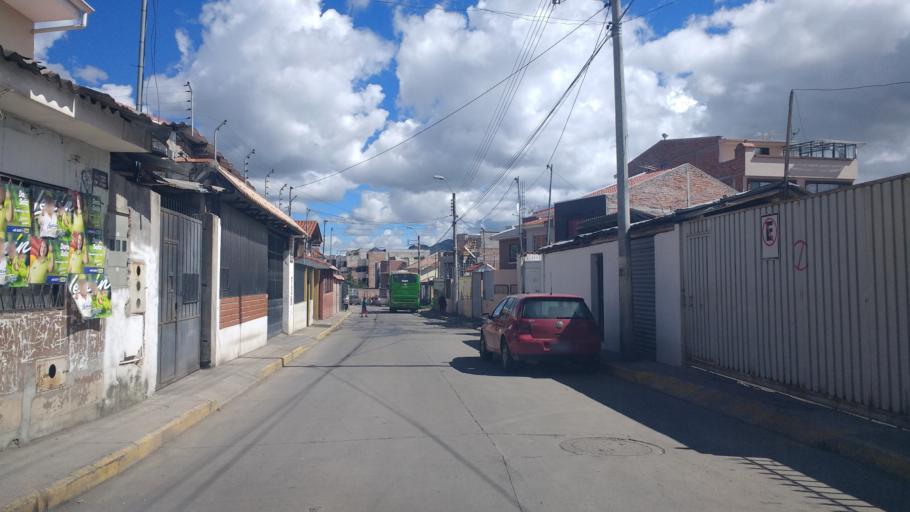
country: EC
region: Azuay
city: Cuenca
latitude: -2.8959
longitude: -79.0350
